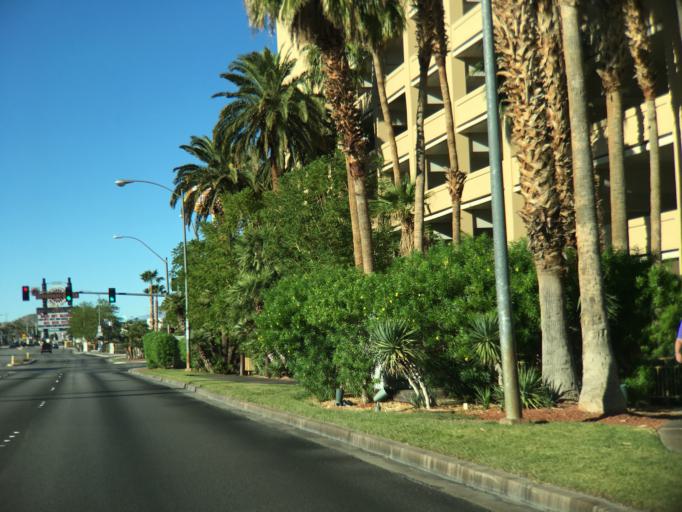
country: US
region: Arizona
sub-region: Mohave County
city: Bullhead City
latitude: 35.1534
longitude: -114.5747
